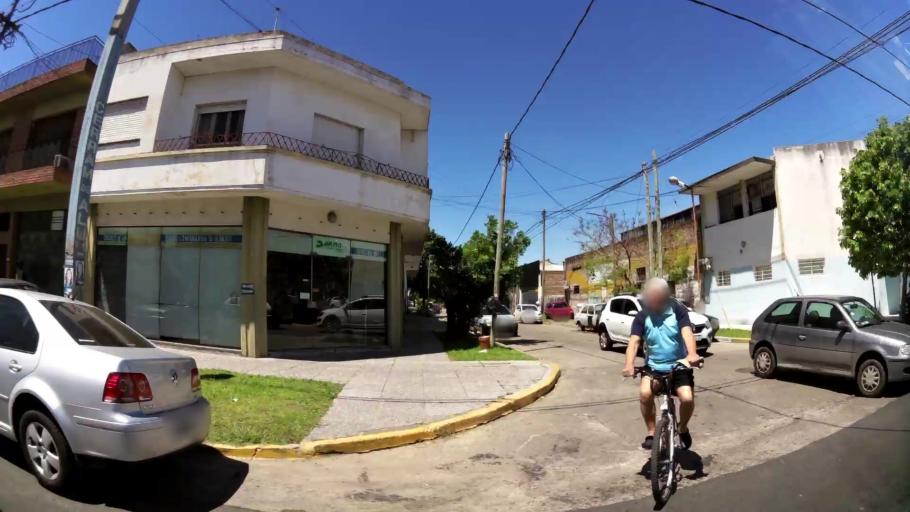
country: AR
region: Buenos Aires
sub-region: Partido de Quilmes
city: Quilmes
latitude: -34.7250
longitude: -58.2733
